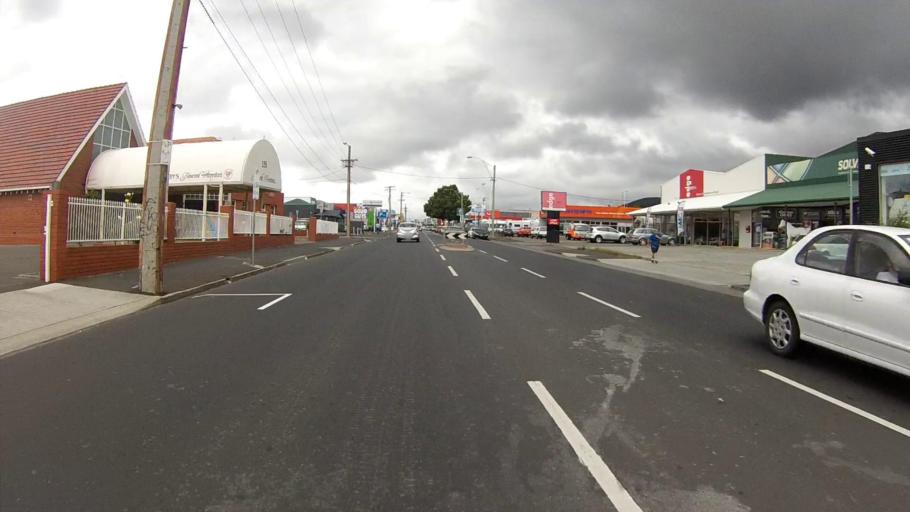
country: AU
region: Tasmania
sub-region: Glenorchy
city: Moonah
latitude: -42.8434
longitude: 147.2926
